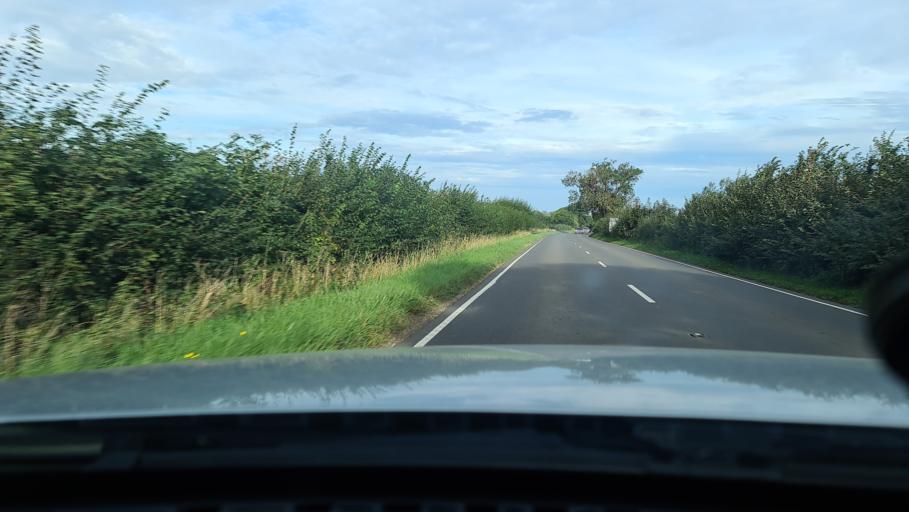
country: GB
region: England
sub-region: Warwickshire
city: Wellesbourne Mountford
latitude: 52.1157
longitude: -1.4901
